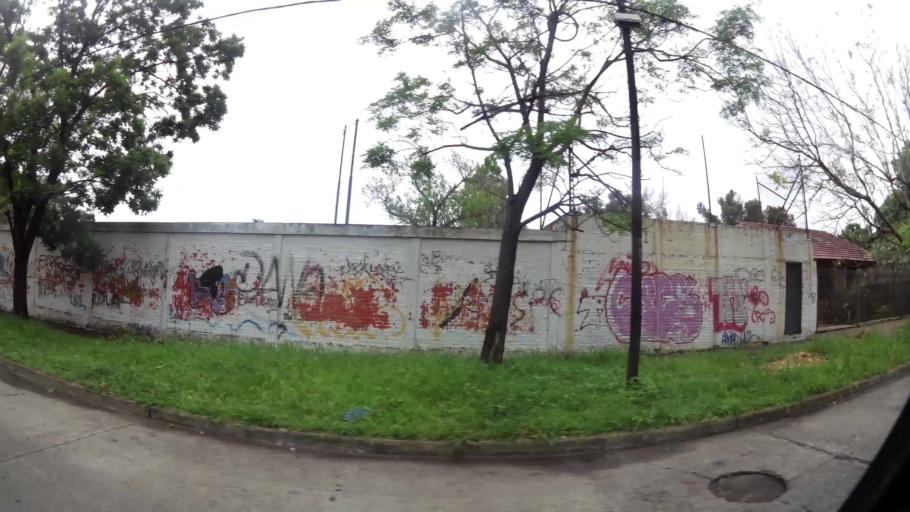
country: AR
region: Buenos Aires
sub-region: Partido de Lomas de Zamora
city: Lomas de Zamora
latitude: -34.7554
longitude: -58.3774
